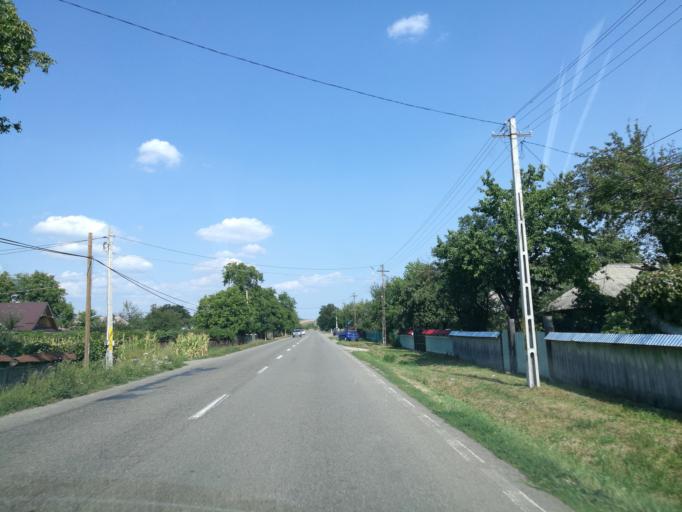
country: RO
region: Neamt
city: Bodesti
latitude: 47.0431
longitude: 26.4063
